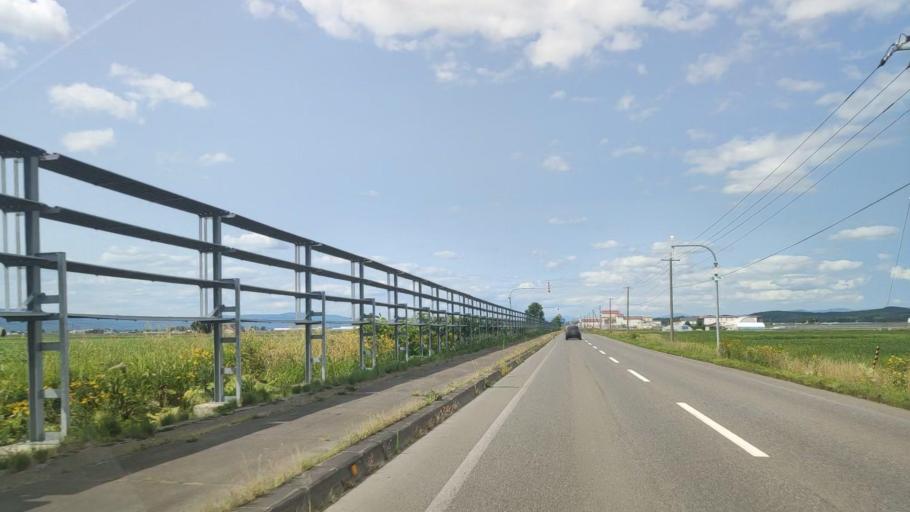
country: JP
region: Hokkaido
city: Nayoro
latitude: 44.1962
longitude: 142.4159
